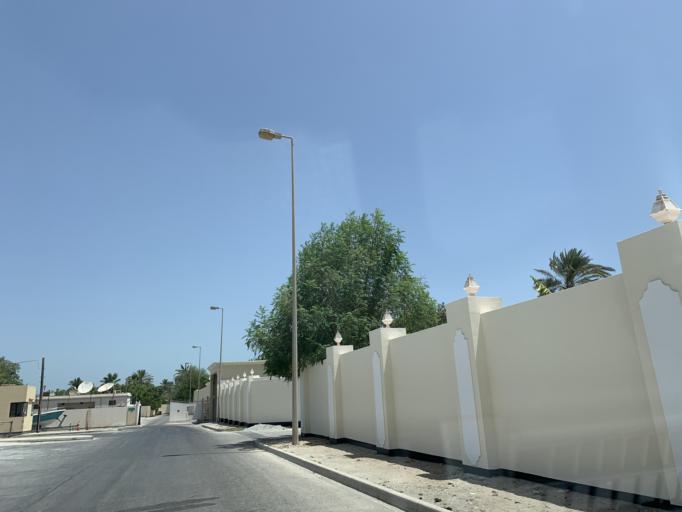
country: BH
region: Manama
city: Jidd Hafs
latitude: 26.2246
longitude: 50.4760
